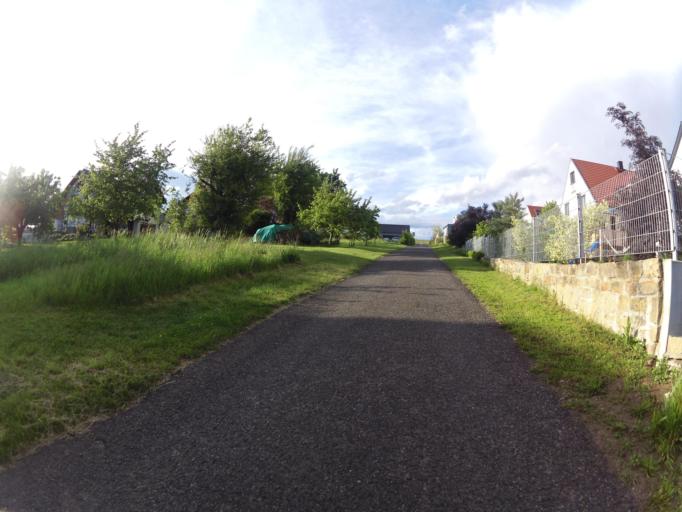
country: DE
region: Bavaria
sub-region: Regierungsbezirk Unterfranken
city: Volkach
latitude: 49.8709
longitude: 10.2307
